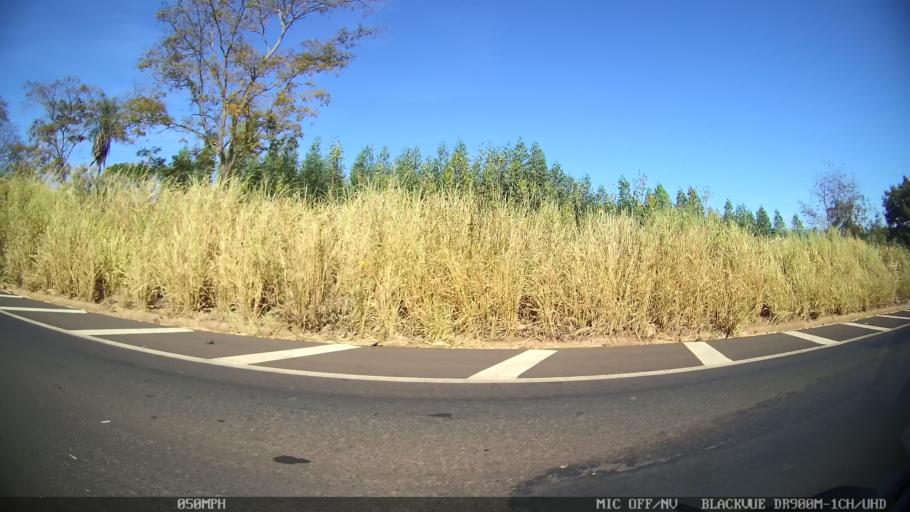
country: BR
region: Sao Paulo
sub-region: Barretos
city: Barretos
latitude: -20.6070
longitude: -48.7430
